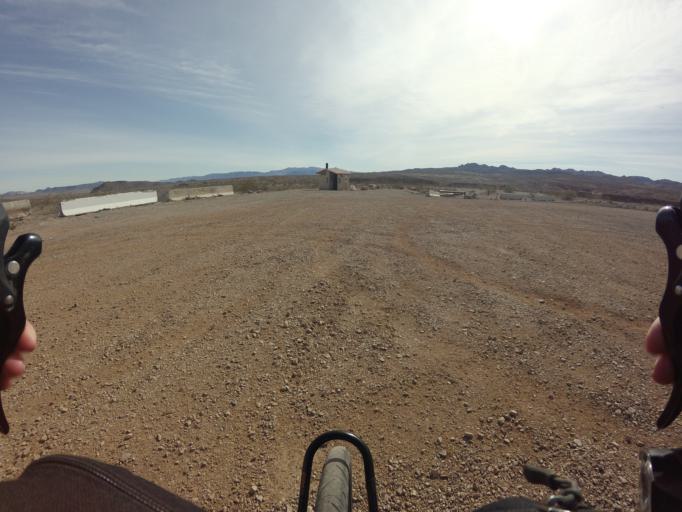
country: US
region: Nevada
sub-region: Clark County
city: Henderson
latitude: 36.1251
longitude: -114.9030
